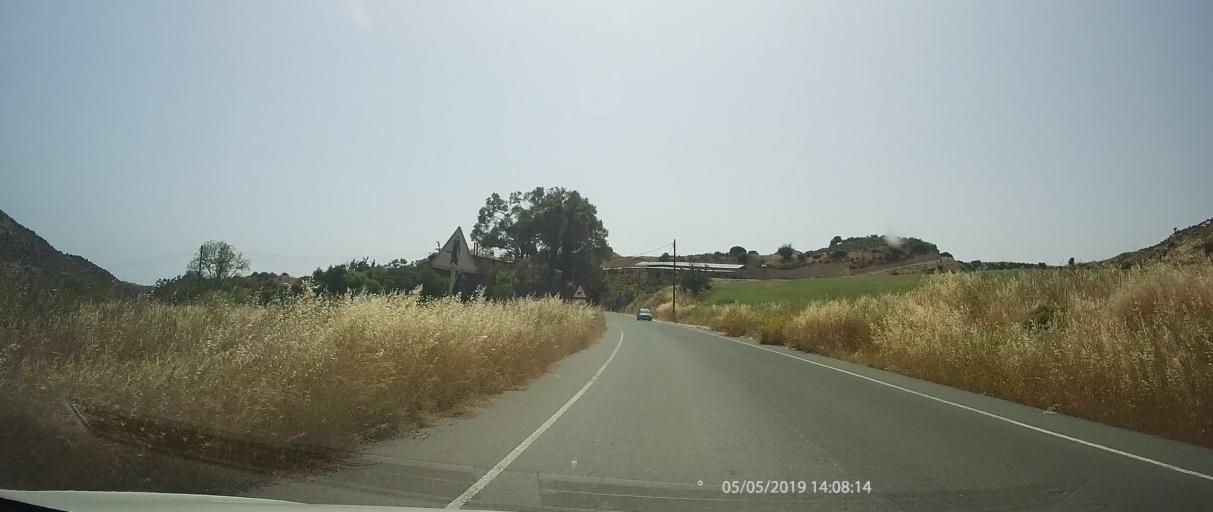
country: CY
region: Limassol
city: Pissouri
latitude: 34.7330
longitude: 32.5861
